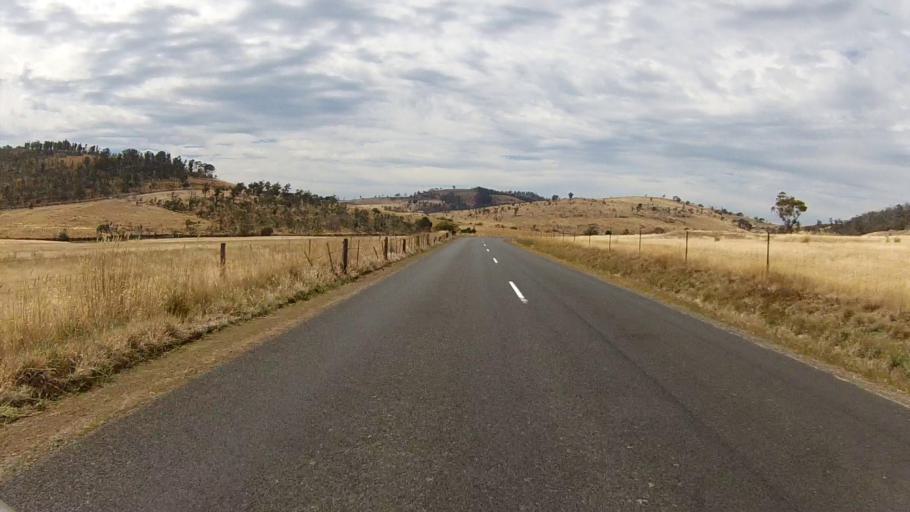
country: AU
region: Tasmania
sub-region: Sorell
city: Sorell
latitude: -42.8713
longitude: 147.6882
